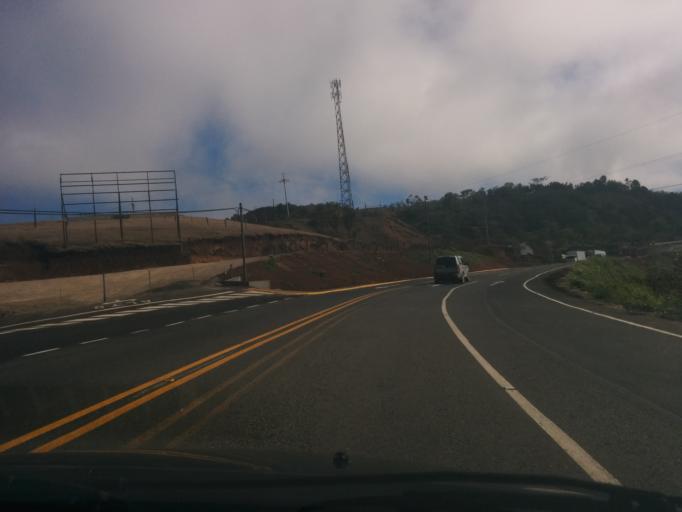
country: CR
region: Alajuela
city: San Rafael
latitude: 10.0663
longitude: -84.4995
